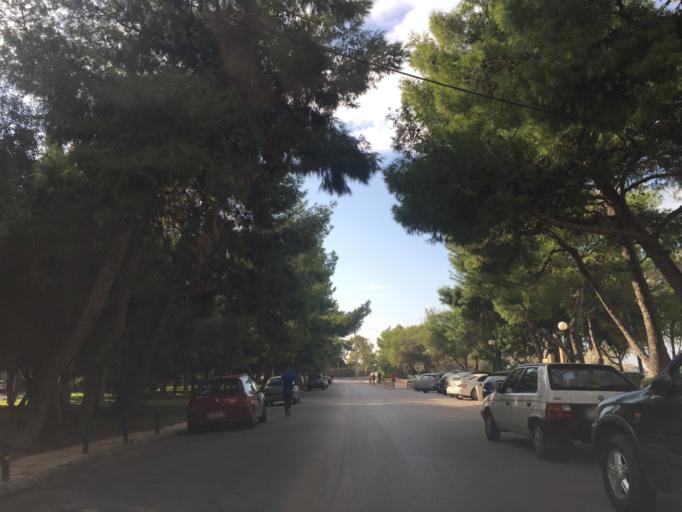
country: GR
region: Attica
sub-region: Nomarchia Anatolikis Attikis
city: Vouliagmeni
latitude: 37.8253
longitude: 23.7706
